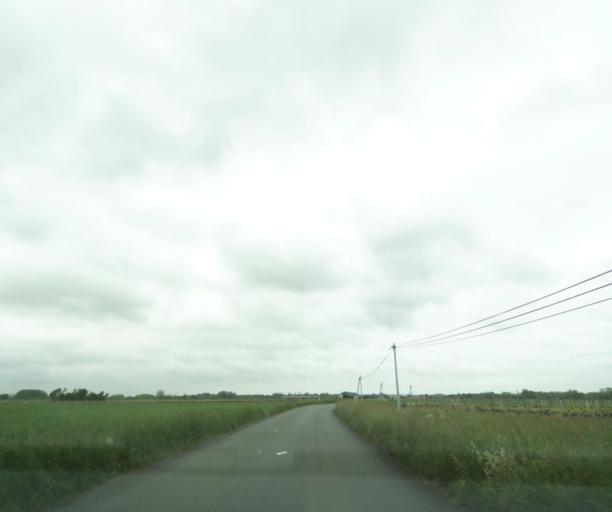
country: FR
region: Poitou-Charentes
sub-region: Departement de la Charente-Maritime
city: Chaniers
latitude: 45.7042
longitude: -0.5627
